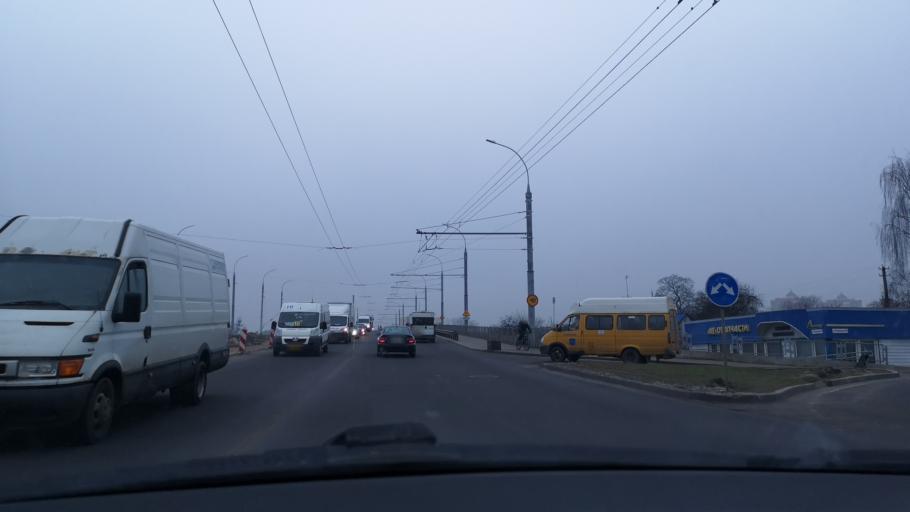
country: BY
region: Brest
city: Brest
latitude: 52.0909
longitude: 23.7186
